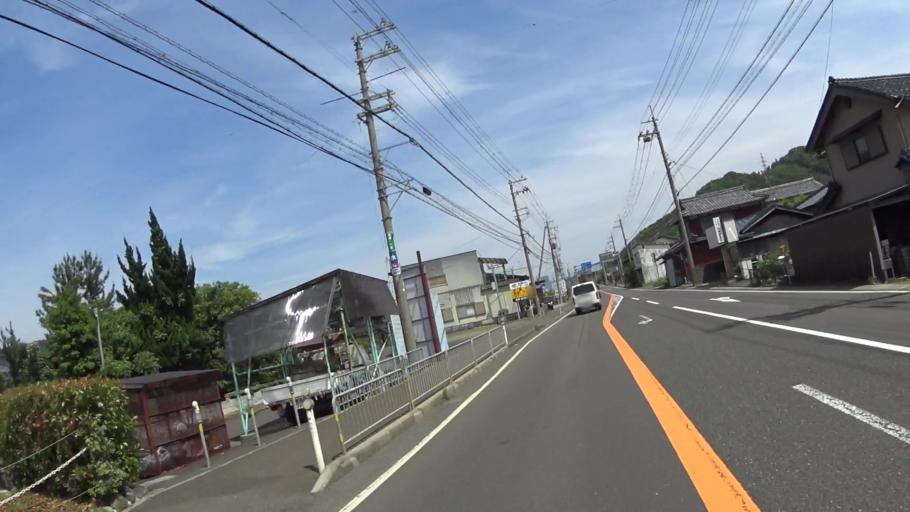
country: JP
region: Fukui
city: Obama
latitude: 35.4823
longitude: 135.7813
